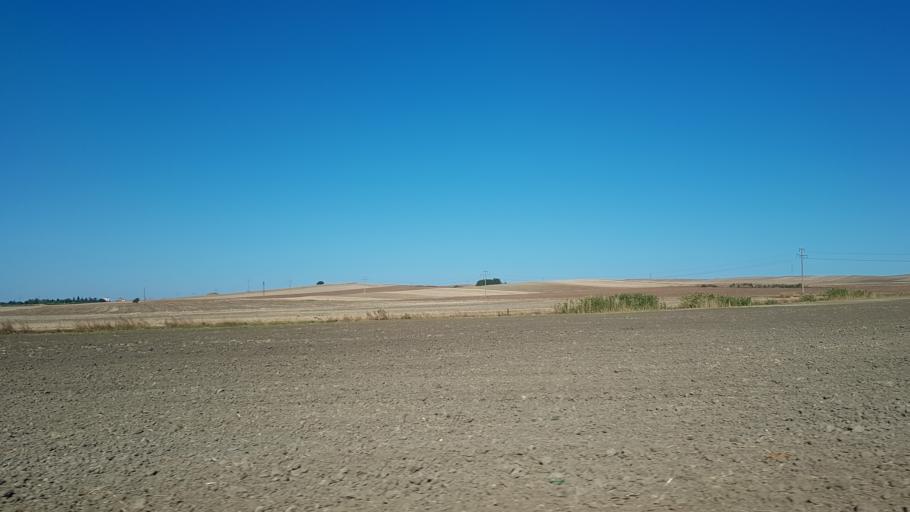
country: TR
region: Tekirdag
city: Corlu
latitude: 41.0110
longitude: 27.8000
